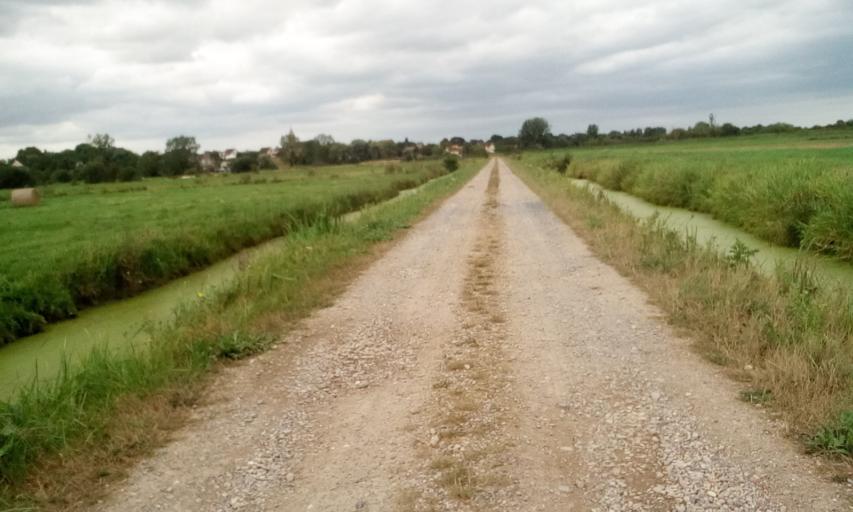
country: FR
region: Lower Normandy
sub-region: Departement du Calvados
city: Troarn
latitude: 49.1943
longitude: -0.1685
